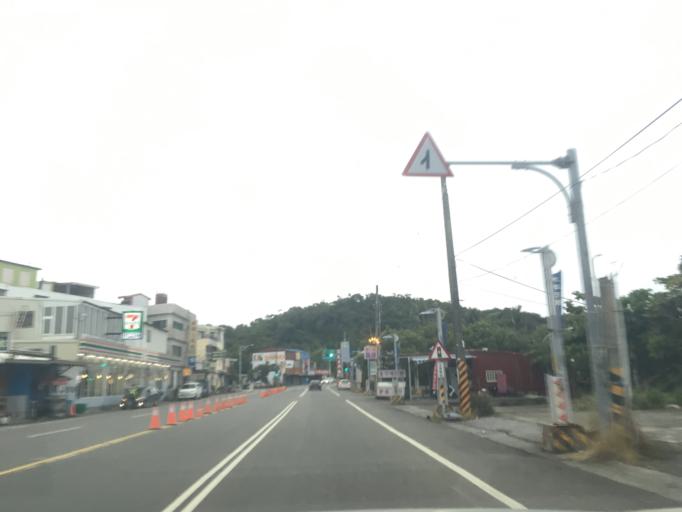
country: TW
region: Taiwan
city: Hengchun
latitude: 22.3392
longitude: 120.8932
